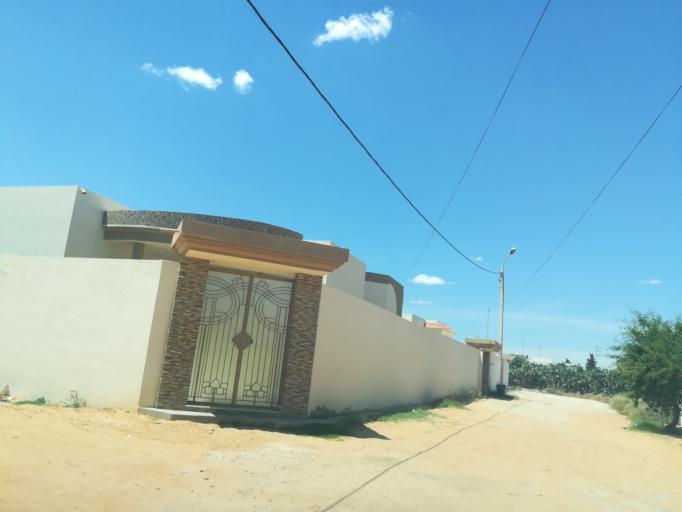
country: TN
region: Safaqis
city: Al Qarmadah
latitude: 34.8161
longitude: 10.7596
